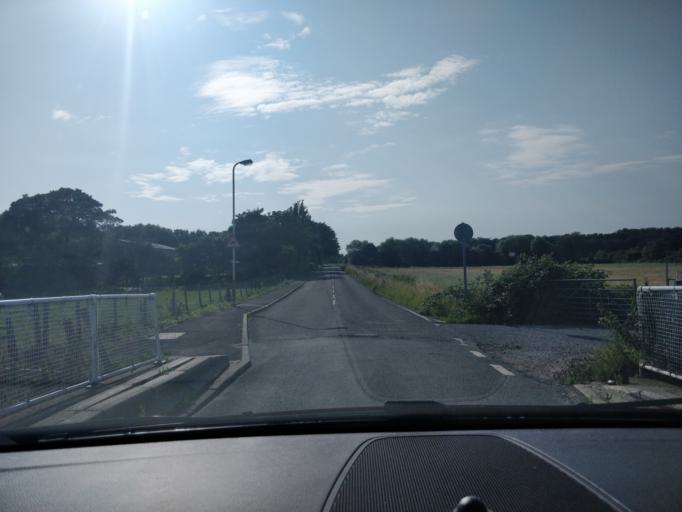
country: GB
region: England
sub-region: Lancashire
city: Banks
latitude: 53.6524
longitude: -2.9500
